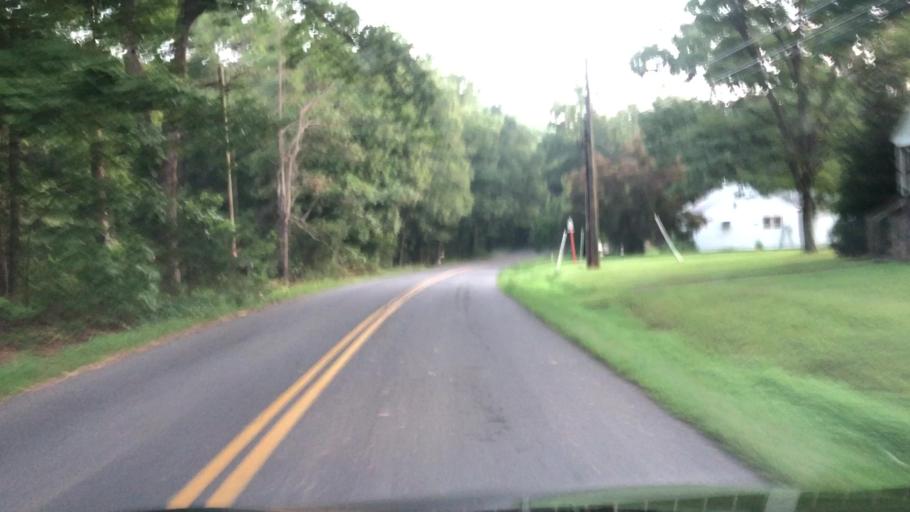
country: US
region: Virginia
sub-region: Prince William County
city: Nokesville
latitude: 38.6910
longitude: -77.6697
